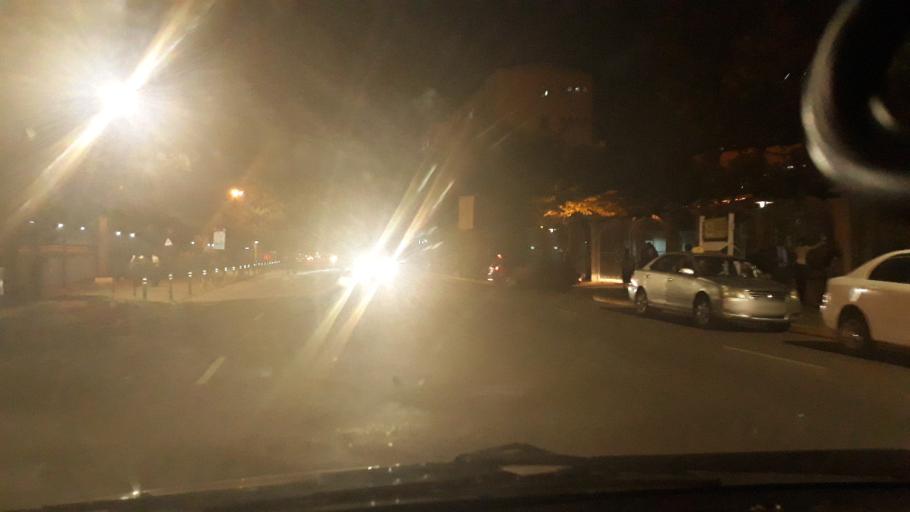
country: KE
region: Nairobi Area
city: Nairobi
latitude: -1.2891
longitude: 36.8241
